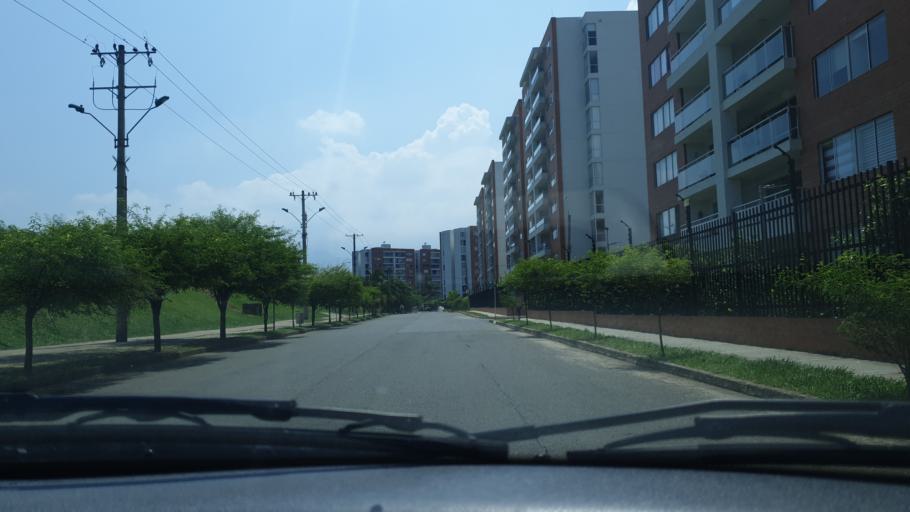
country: CO
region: Valle del Cauca
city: Cali
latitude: 3.3645
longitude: -76.5210
